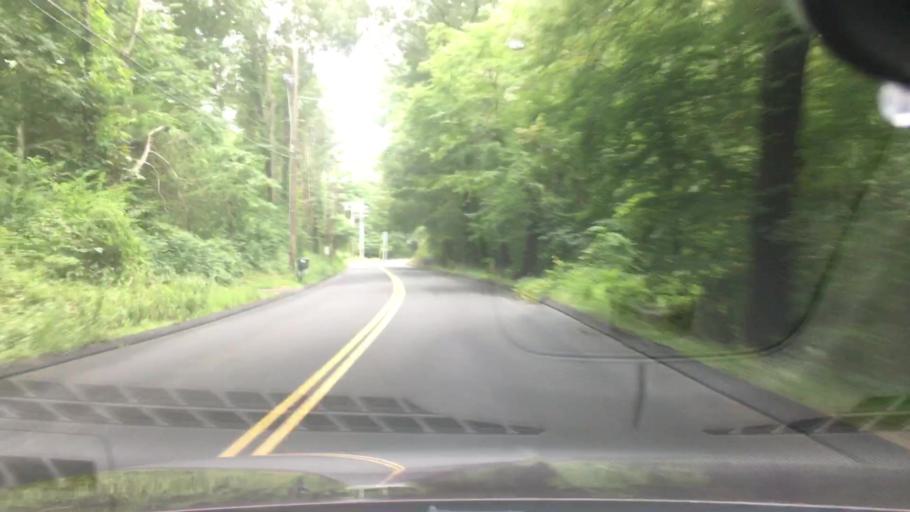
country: US
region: Connecticut
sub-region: New Haven County
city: Madison
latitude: 41.3204
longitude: -72.5944
